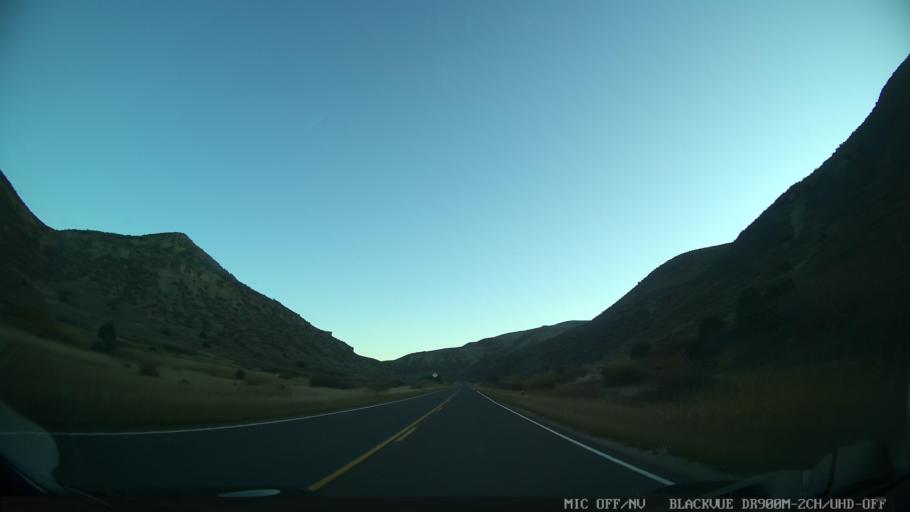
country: US
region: Colorado
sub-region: Eagle County
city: Edwards
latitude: 39.7754
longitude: -106.6830
